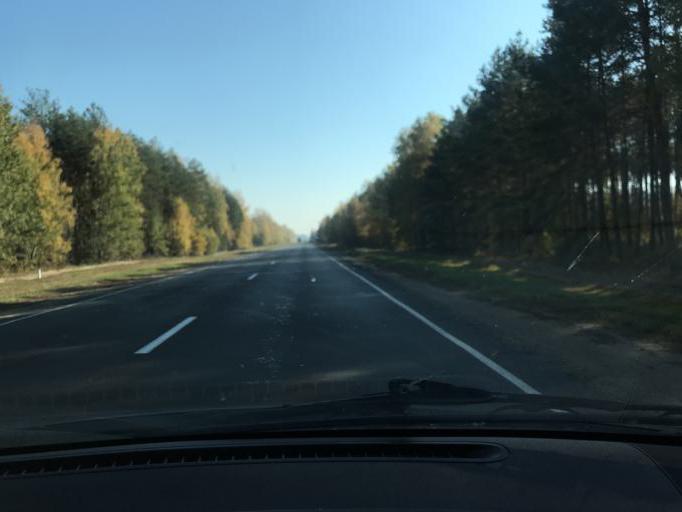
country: BY
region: Brest
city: Luninyets
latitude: 52.2720
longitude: 26.9893
